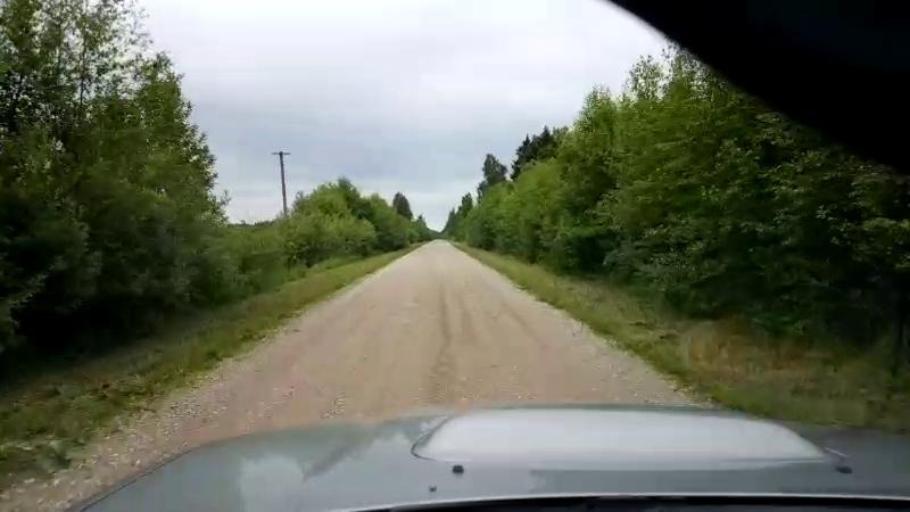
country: EE
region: Paernumaa
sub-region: Halinga vald
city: Parnu-Jaagupi
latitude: 58.5602
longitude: 24.5632
